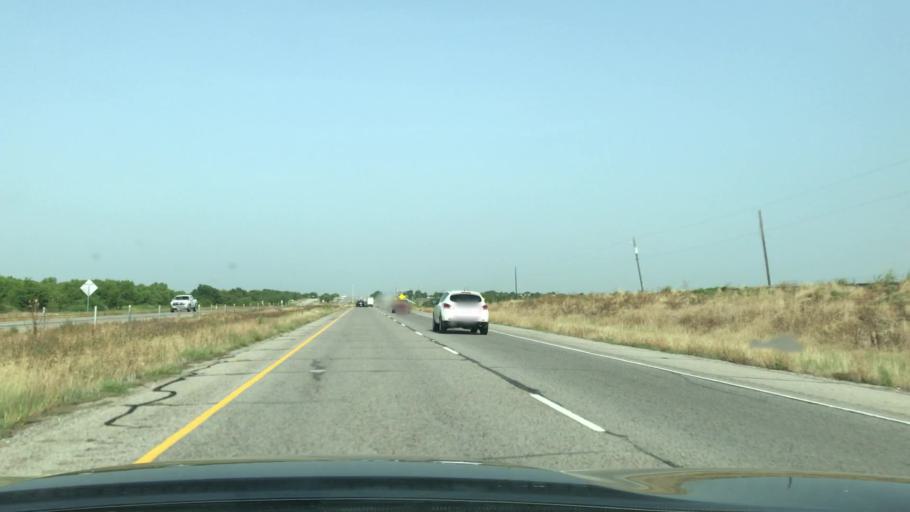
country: US
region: Texas
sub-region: Kaufman County
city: Talty
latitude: 32.7398
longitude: -96.3860
